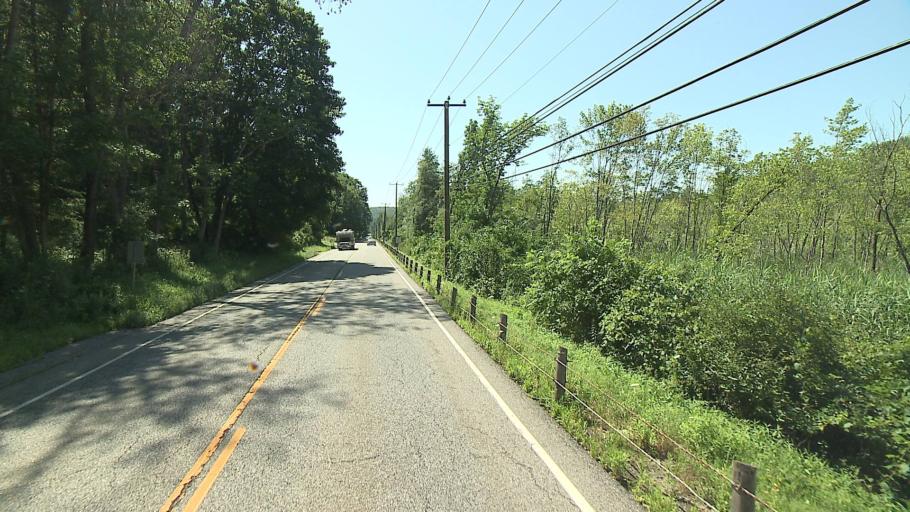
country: US
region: Connecticut
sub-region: Litchfield County
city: Kent
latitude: 41.8710
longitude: -73.4648
